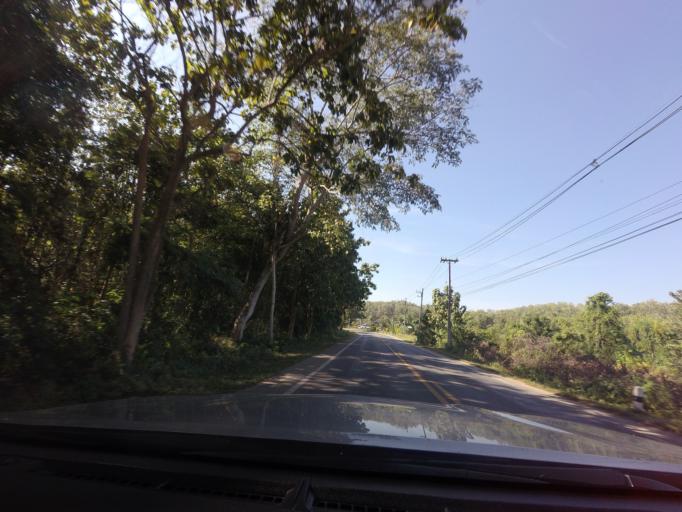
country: TH
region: Sukhothai
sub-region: Amphoe Si Satchanalai
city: Si Satchanalai
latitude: 17.6302
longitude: 99.6985
